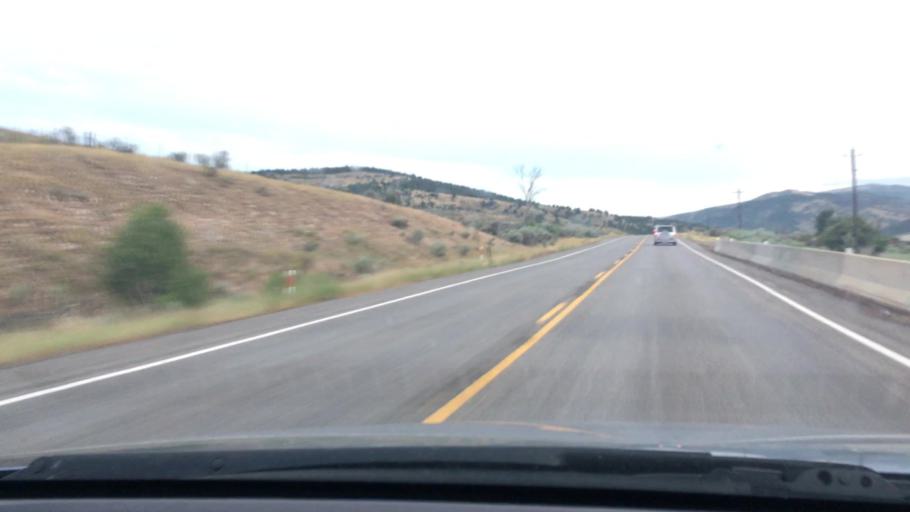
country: US
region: Utah
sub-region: Utah County
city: Woodland Hills
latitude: 39.9097
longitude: -111.5498
